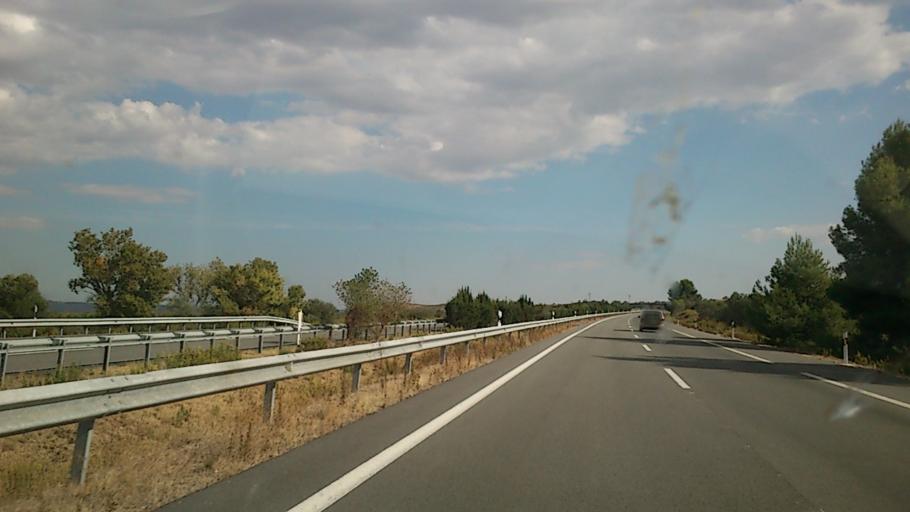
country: ES
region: La Rioja
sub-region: Provincia de La Rioja
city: Pradejon
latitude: 42.3340
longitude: -2.0159
